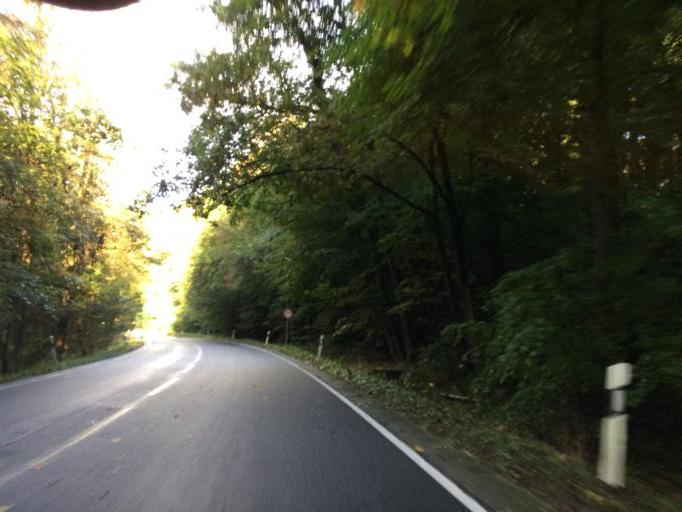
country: DE
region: North Rhine-Westphalia
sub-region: Regierungsbezirk Koln
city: Konigswinter
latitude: 50.6798
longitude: 7.2232
